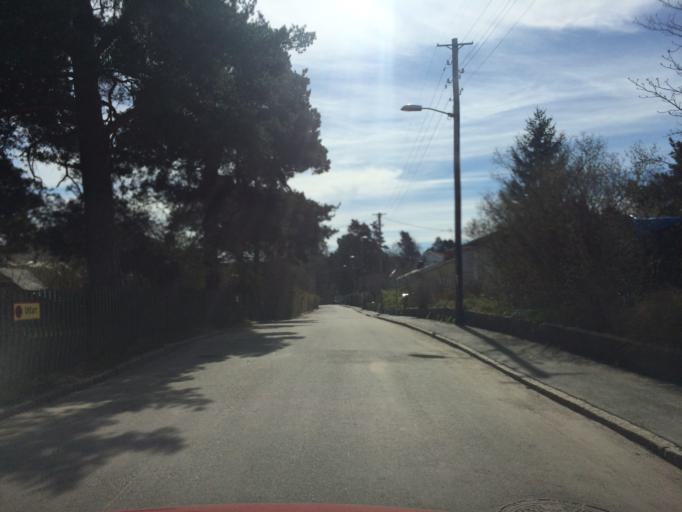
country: SE
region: Stockholm
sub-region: Huddinge Kommun
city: Huddinge
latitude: 59.2826
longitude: 17.9880
